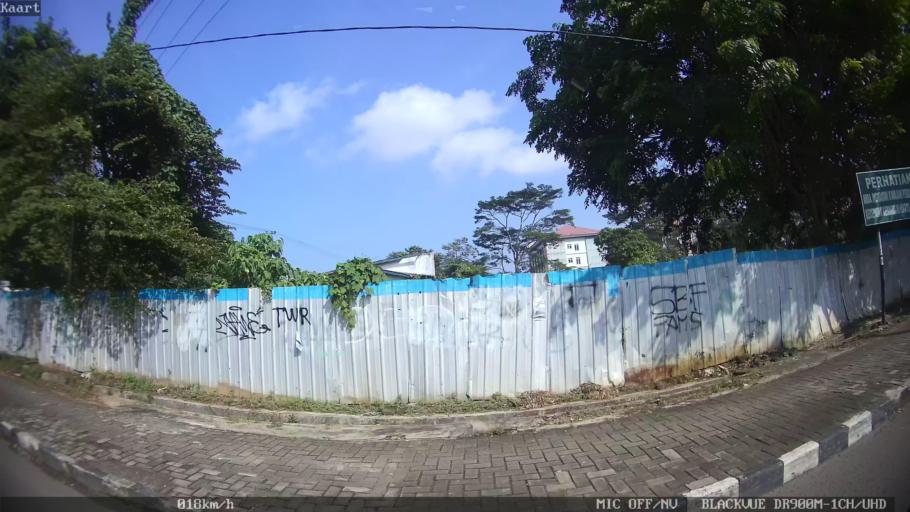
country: ID
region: Lampung
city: Kedaton
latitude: -5.3716
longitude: 105.2396
